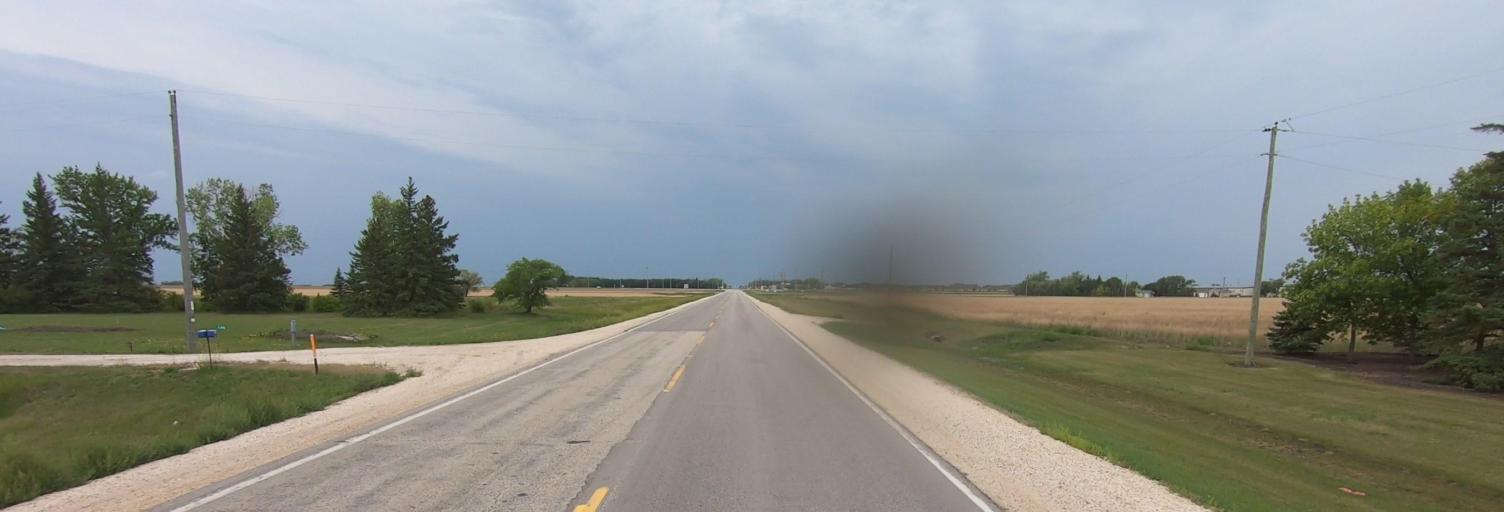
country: CA
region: Manitoba
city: Headingley
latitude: 49.7683
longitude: -97.3167
